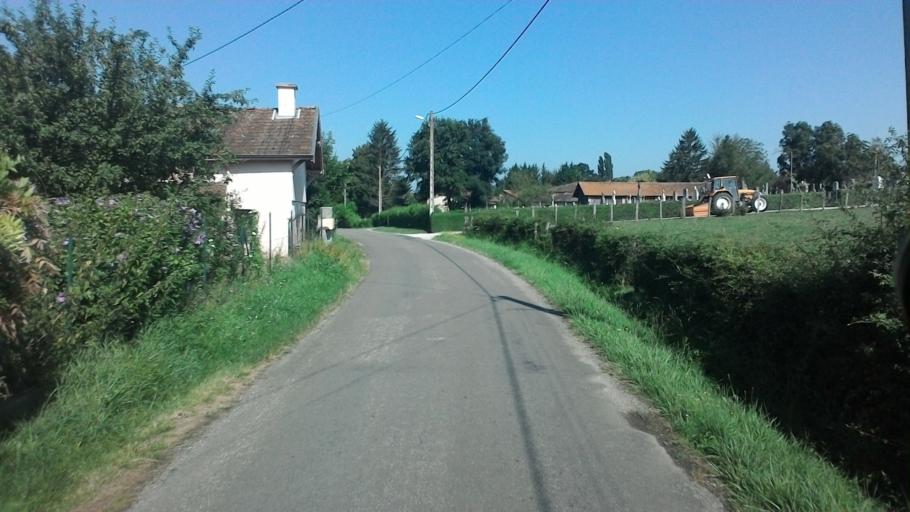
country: FR
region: Rhone-Alpes
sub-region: Departement de l'Ain
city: Saint-Trivier-de-Courtes
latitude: 46.4026
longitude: 5.1118
